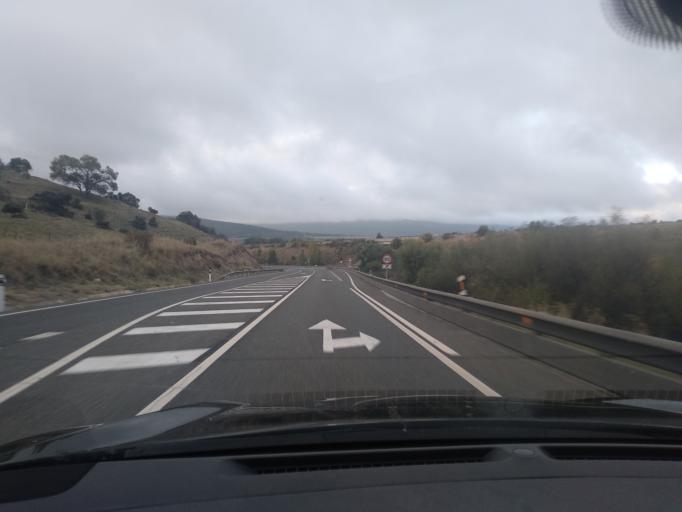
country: ES
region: Castille and Leon
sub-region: Provincia de Segovia
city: Otero de Herreros
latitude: 40.7602
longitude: -4.2108
